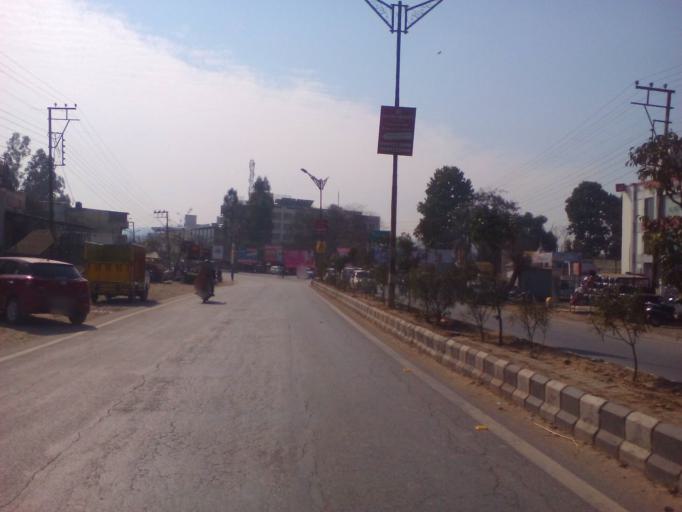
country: IN
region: Uttarakhand
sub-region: Dehradun
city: Clement Town
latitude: 30.2788
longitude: 77.9906
